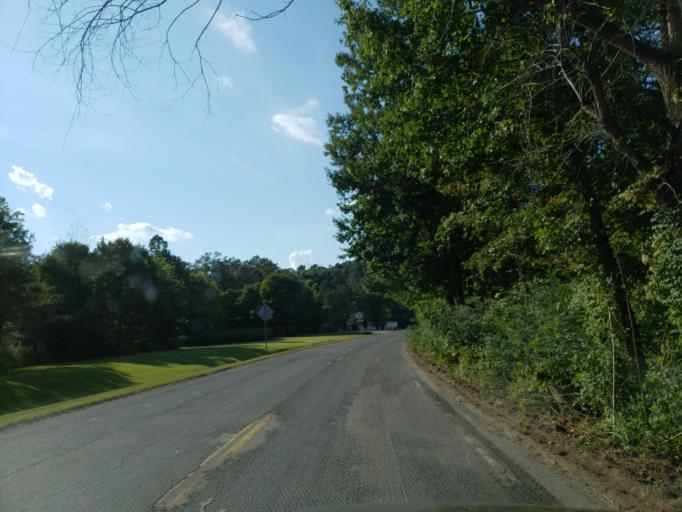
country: US
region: Georgia
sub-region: Cobb County
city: Powder Springs
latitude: 33.8702
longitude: -84.7114
